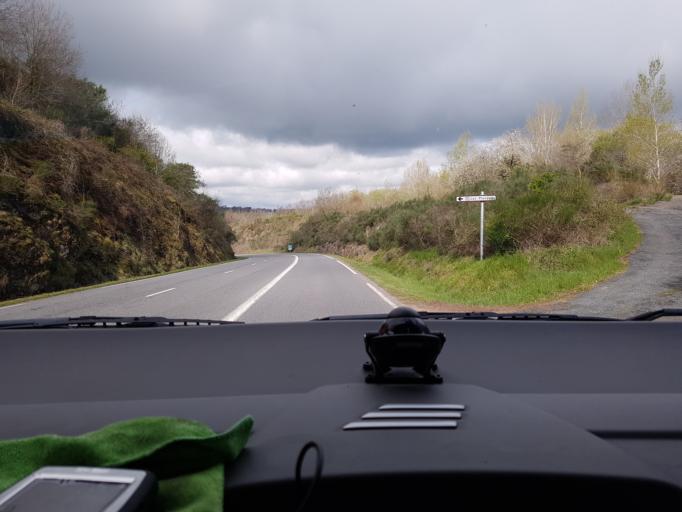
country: FR
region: Midi-Pyrenees
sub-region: Departement de l'Aveyron
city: Moyrazes
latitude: 44.3819
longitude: 2.4224
